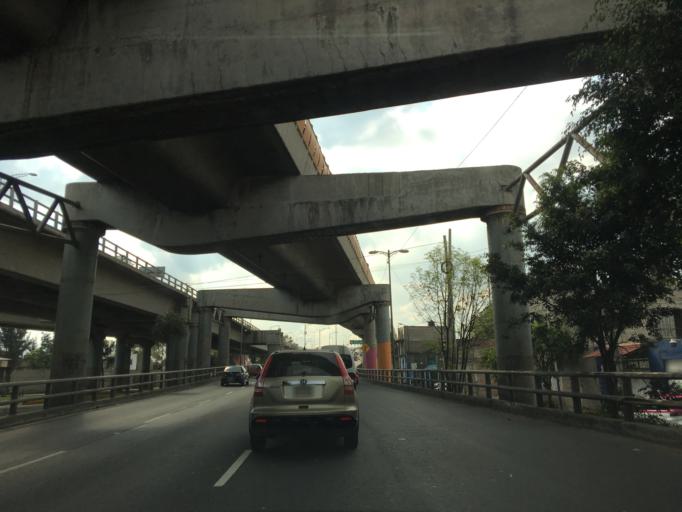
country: MX
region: Mexico City
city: Venustiano Carranza
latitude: 19.4355
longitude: -99.1064
